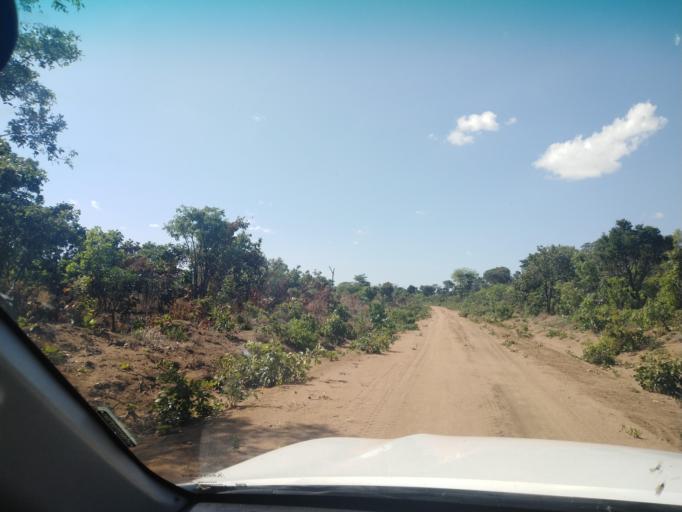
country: ZM
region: Northern
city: Chinsali
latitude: -11.0047
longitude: 31.7742
